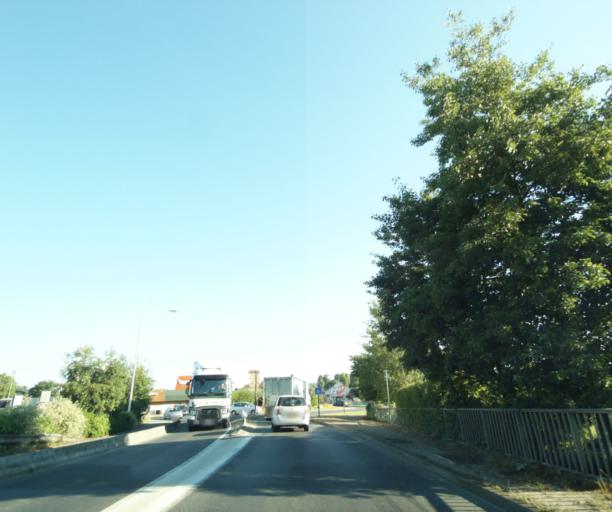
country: FR
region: Ile-de-France
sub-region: Departement de Seine-et-Marne
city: Montereau-Fault-Yonne
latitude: 48.3753
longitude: 2.9575
